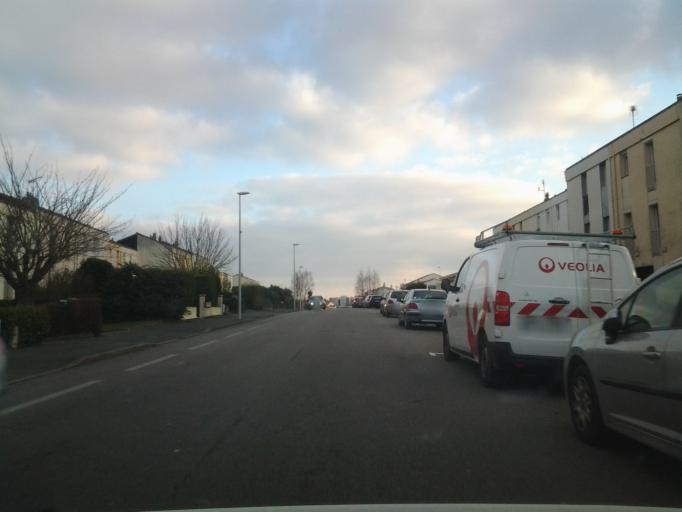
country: FR
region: Pays de la Loire
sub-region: Departement de la Vendee
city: La Roche-sur-Yon
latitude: 46.6847
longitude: -1.4234
